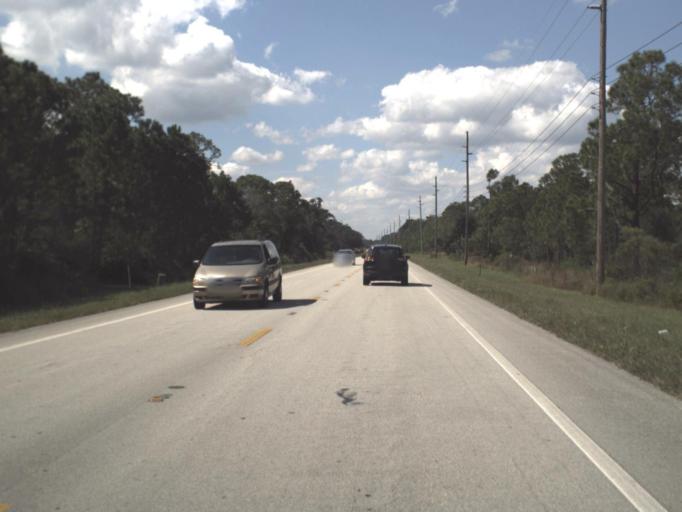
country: US
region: Florida
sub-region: Highlands County
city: Sebring
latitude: 27.4306
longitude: -81.3882
